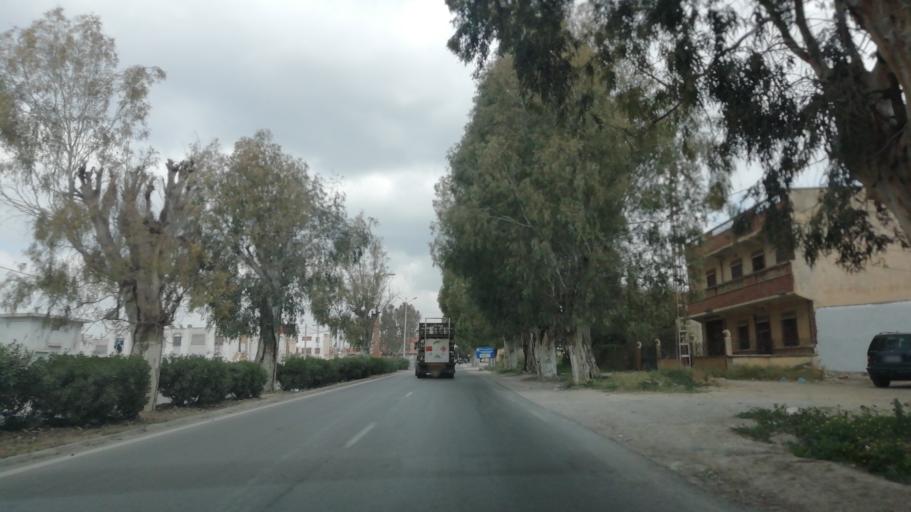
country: DZ
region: Mascara
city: Mascara
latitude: 35.6174
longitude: 0.1088
